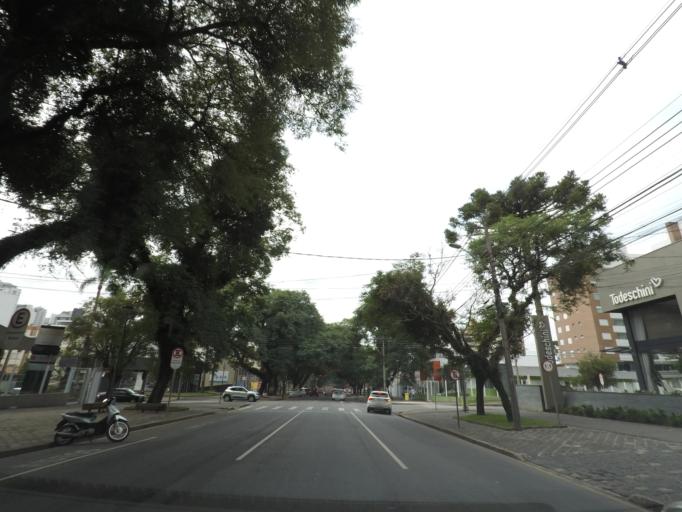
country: BR
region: Parana
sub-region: Curitiba
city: Curitiba
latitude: -25.4496
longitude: -49.2838
